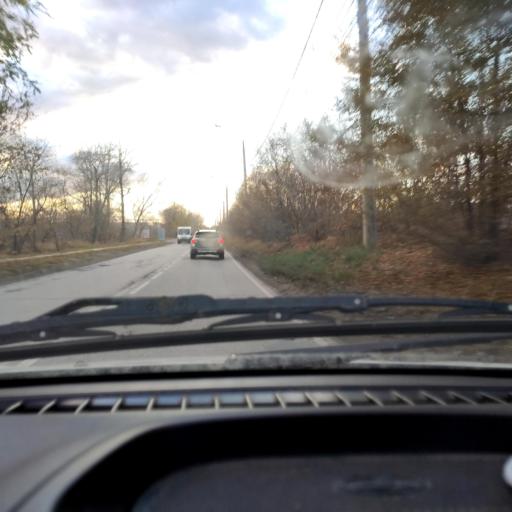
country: RU
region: Samara
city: Zhigulevsk
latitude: 53.4636
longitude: 49.5586
